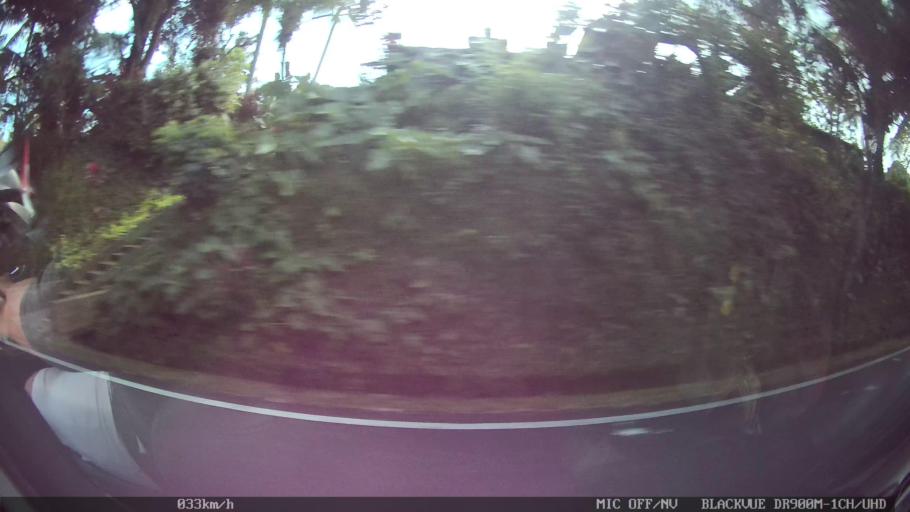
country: ID
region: Bali
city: Banjar Pesalakan
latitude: -8.4974
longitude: 115.2972
